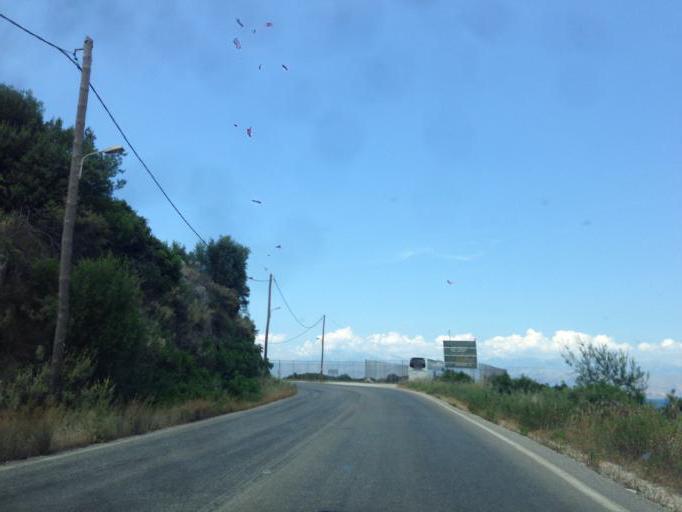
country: GR
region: Ionian Islands
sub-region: Nomos Kerkyras
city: Acharavi
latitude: 39.7898
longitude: 19.9089
